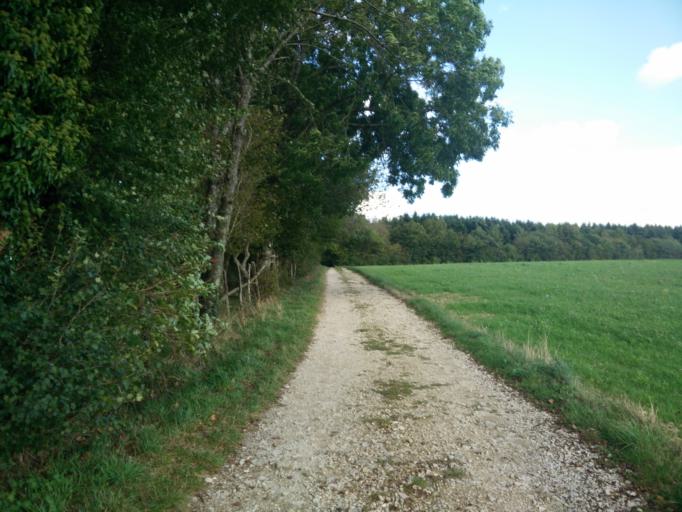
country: FR
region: Franche-Comte
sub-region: Departement du Doubs
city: Saone
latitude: 47.2202
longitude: 6.1327
